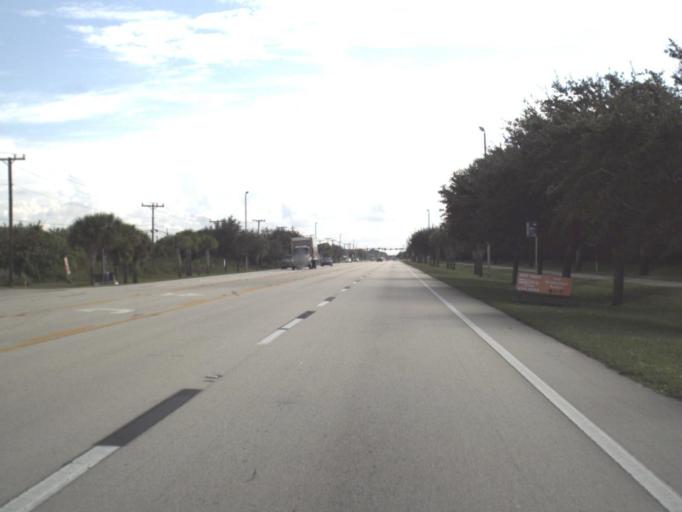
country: US
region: Florida
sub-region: Lee County
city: Fort Myers Shores
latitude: 26.7061
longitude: -81.7393
